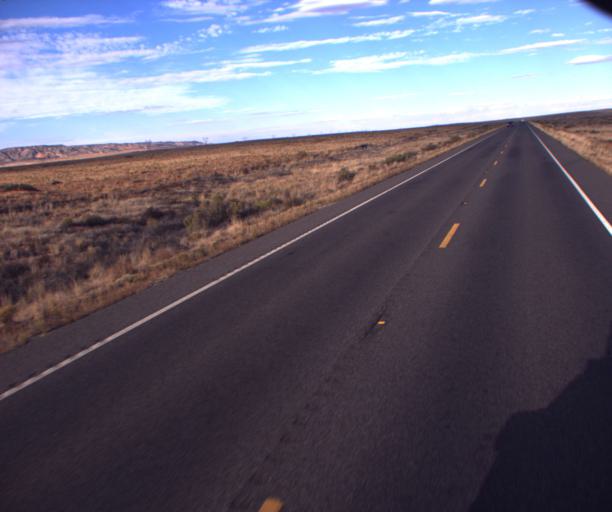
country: US
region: Arizona
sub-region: Apache County
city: Lukachukai
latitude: 36.9457
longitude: -109.2677
